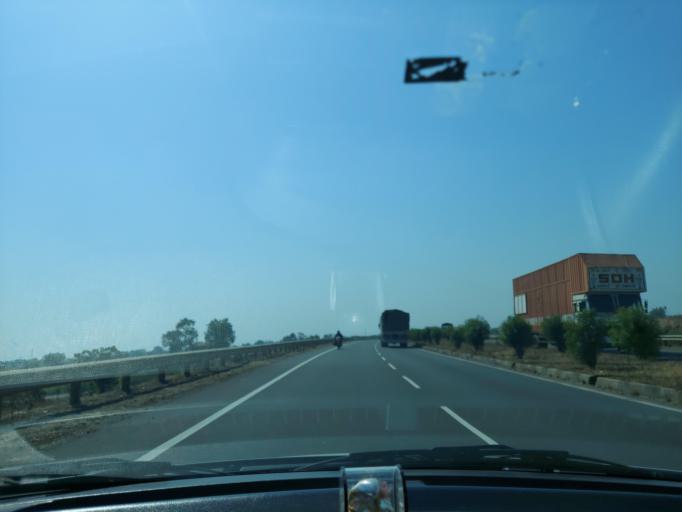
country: IN
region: Madhya Pradesh
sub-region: Dhar
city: Dhamnod
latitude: 22.3005
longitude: 75.5021
